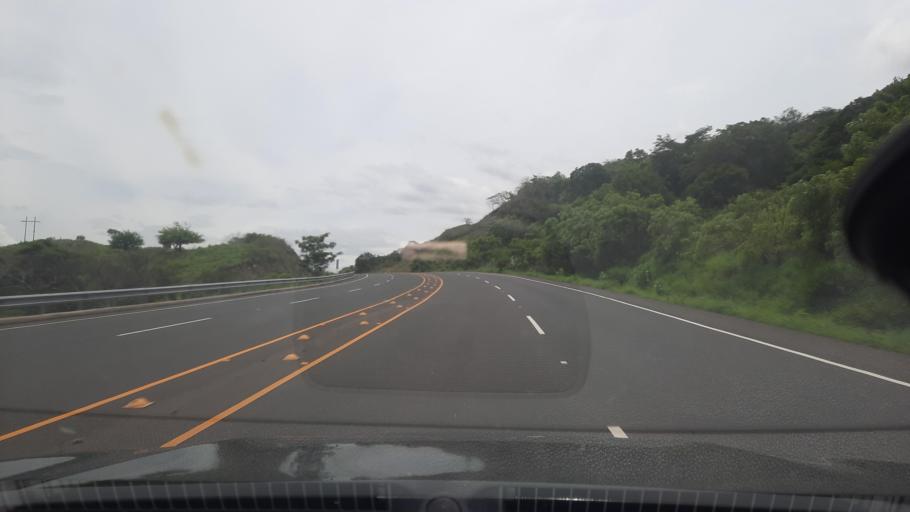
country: HN
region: Valle
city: Aramecina
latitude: 13.7987
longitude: -87.7051
